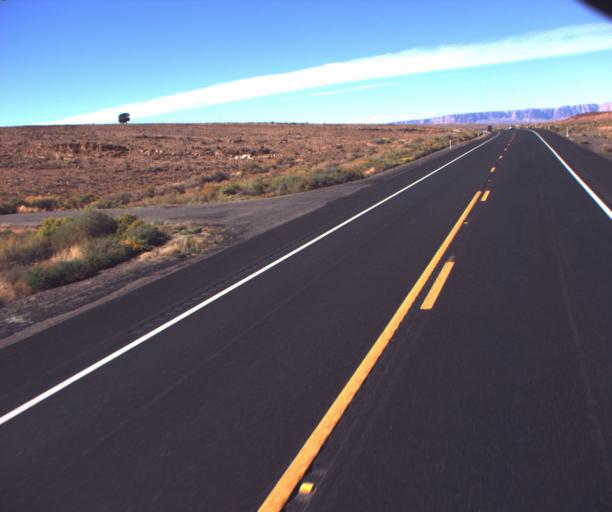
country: US
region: Arizona
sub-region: Coconino County
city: LeChee
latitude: 36.5265
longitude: -111.6027
